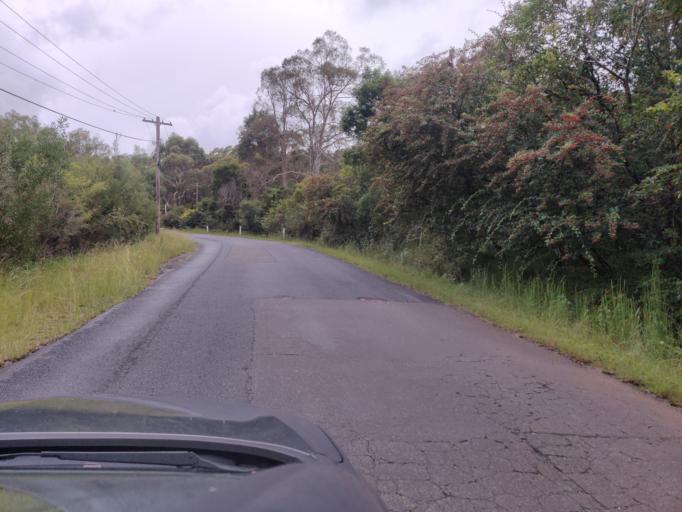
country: AU
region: New South Wales
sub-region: Pittwater
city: Ingleside
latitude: -33.6829
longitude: 151.2530
